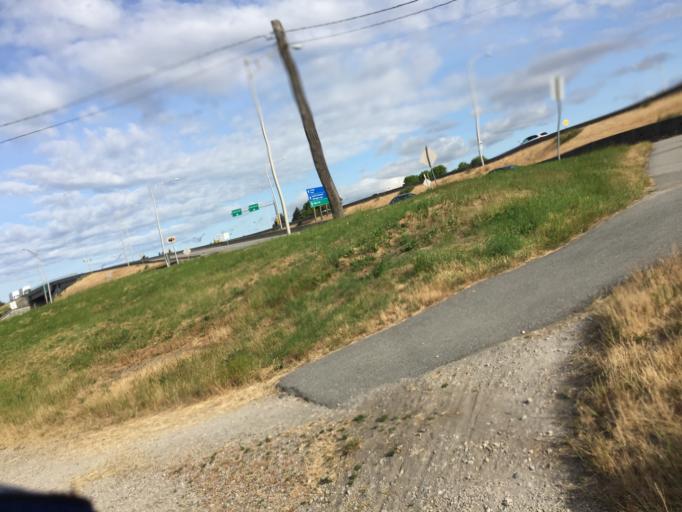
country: CA
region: British Columbia
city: Richmond
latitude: 49.1921
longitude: -123.1392
